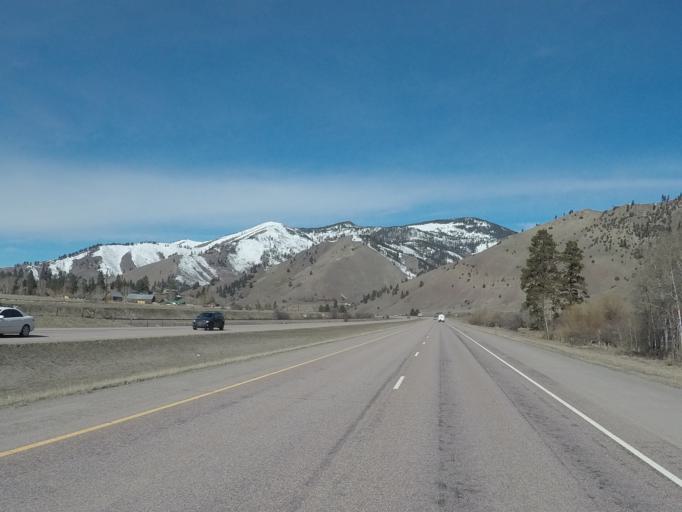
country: US
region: Montana
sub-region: Missoula County
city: Clinton
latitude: 46.7010
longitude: -113.3643
